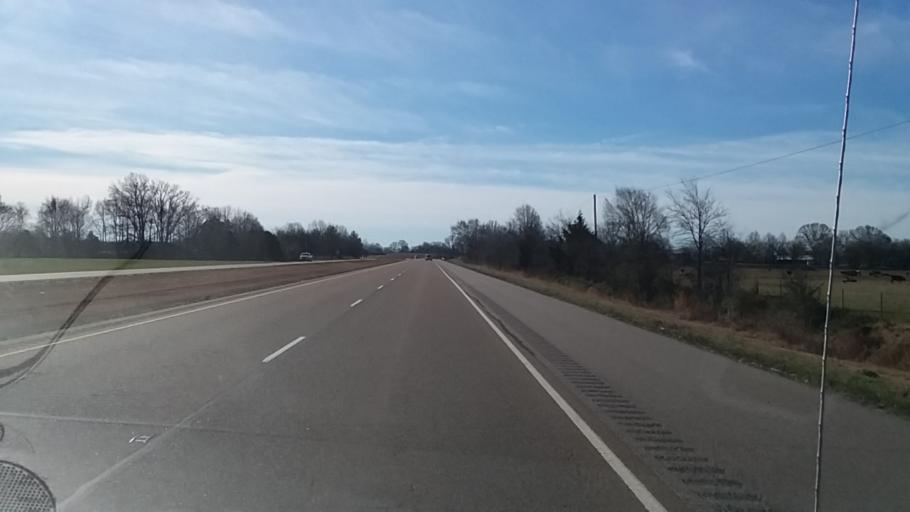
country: US
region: Tennessee
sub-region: Crockett County
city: Alamo
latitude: 35.8436
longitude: -89.1913
